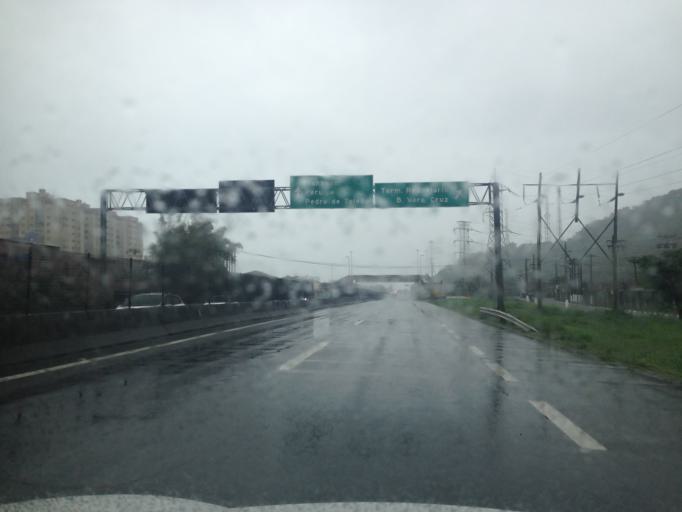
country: BR
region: Sao Paulo
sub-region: Mongagua
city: Mongagua
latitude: -24.0957
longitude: -46.6272
